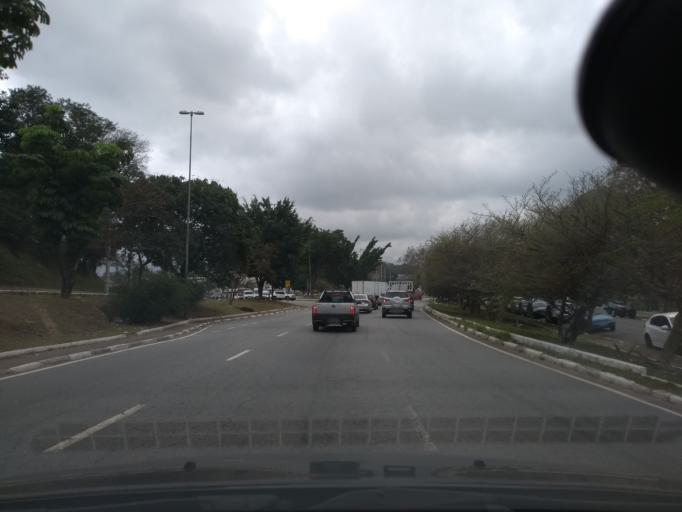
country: BR
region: Sao Paulo
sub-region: Guarulhos
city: Guarulhos
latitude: -23.4596
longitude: -46.4964
